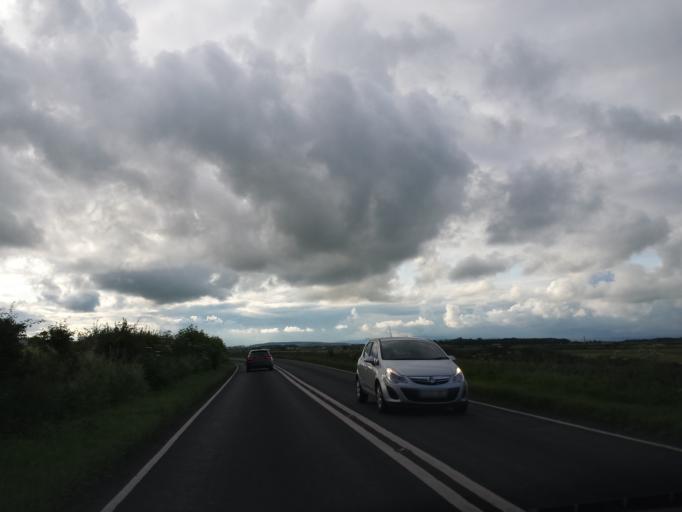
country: GB
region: Scotland
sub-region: Fife
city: Strathkinness
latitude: 56.3548
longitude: -2.8557
